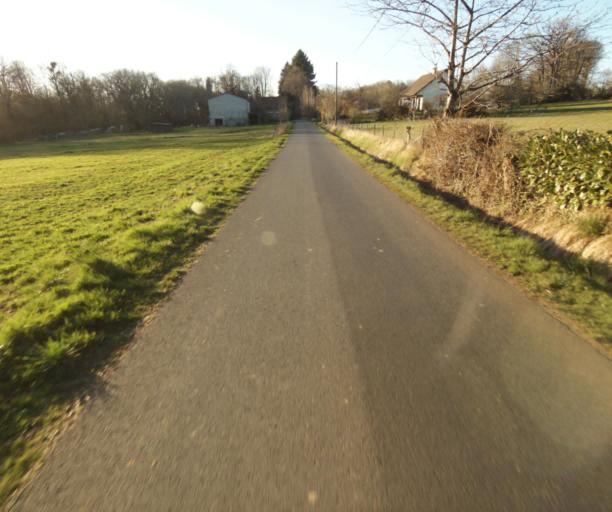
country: FR
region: Limousin
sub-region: Departement de la Correze
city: Seilhac
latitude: 45.3502
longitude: 1.7124
